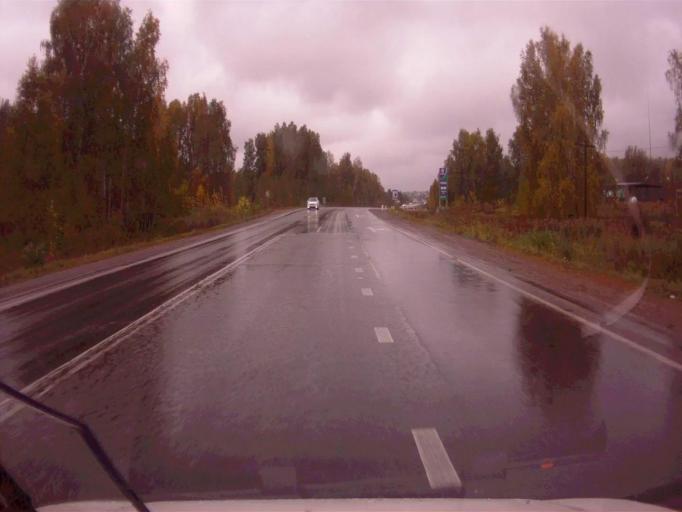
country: RU
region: Chelyabinsk
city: Argayash
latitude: 55.4707
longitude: 60.9027
